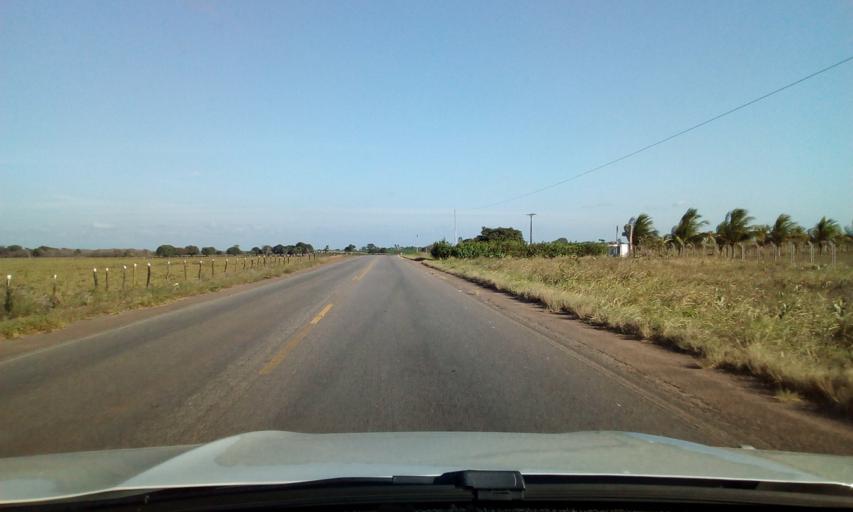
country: BR
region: Paraiba
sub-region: Mari
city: Mari
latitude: -7.0183
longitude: -35.3517
